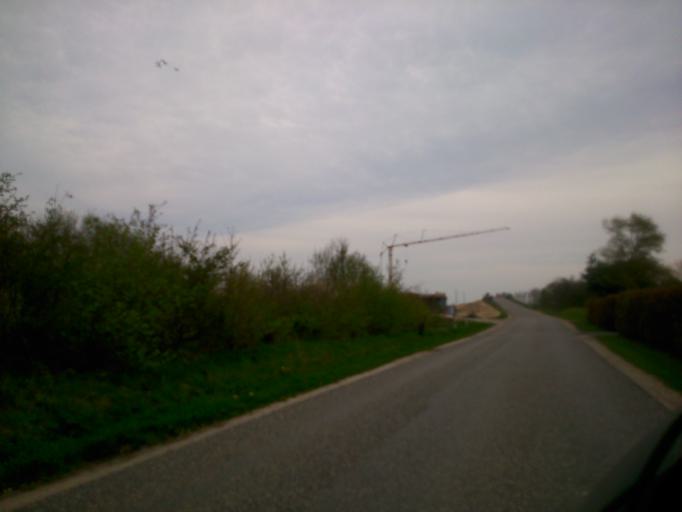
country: DK
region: South Denmark
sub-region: Esbjerg Kommune
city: Bramming
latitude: 55.4677
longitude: 8.6520
